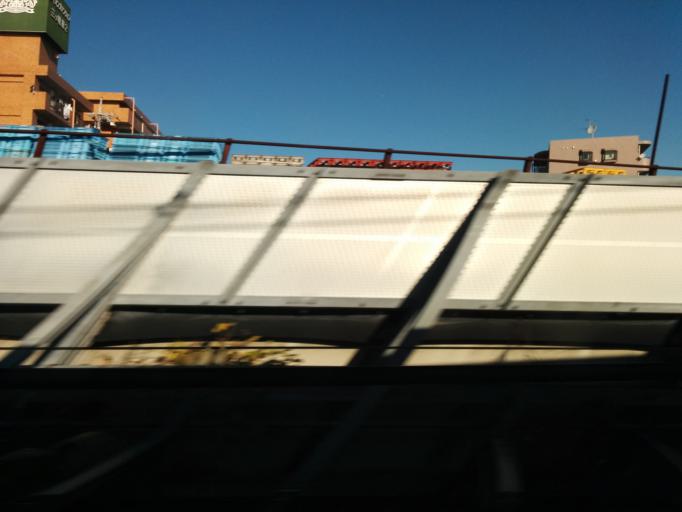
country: JP
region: Kanagawa
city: Minami-rinkan
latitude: 35.4435
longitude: 139.4965
